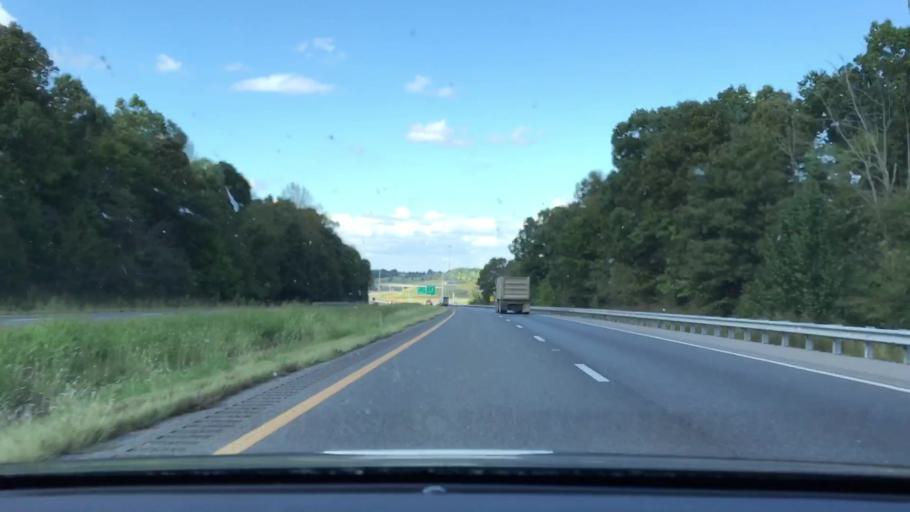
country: US
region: Kentucky
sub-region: Marshall County
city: Calvert City
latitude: 36.9752
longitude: -88.3459
